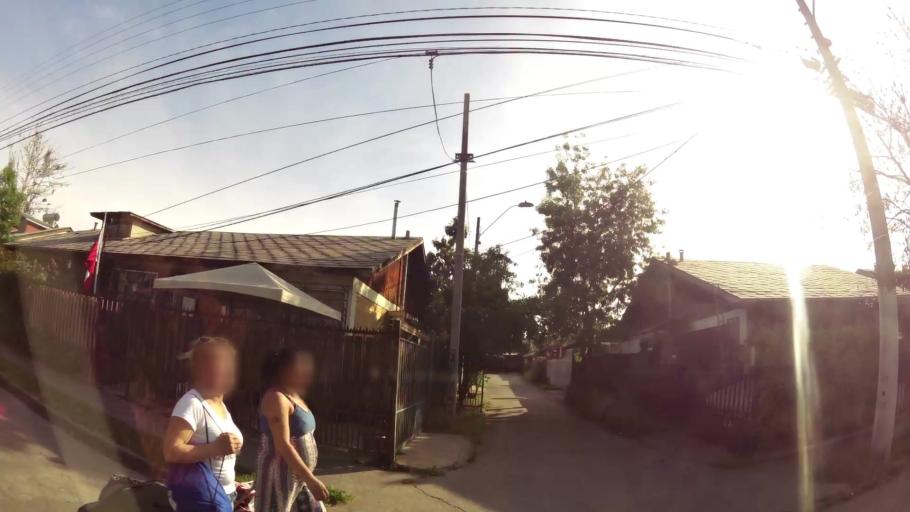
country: CL
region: Santiago Metropolitan
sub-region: Provincia de Santiago
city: La Pintana
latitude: -33.5414
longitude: -70.5849
